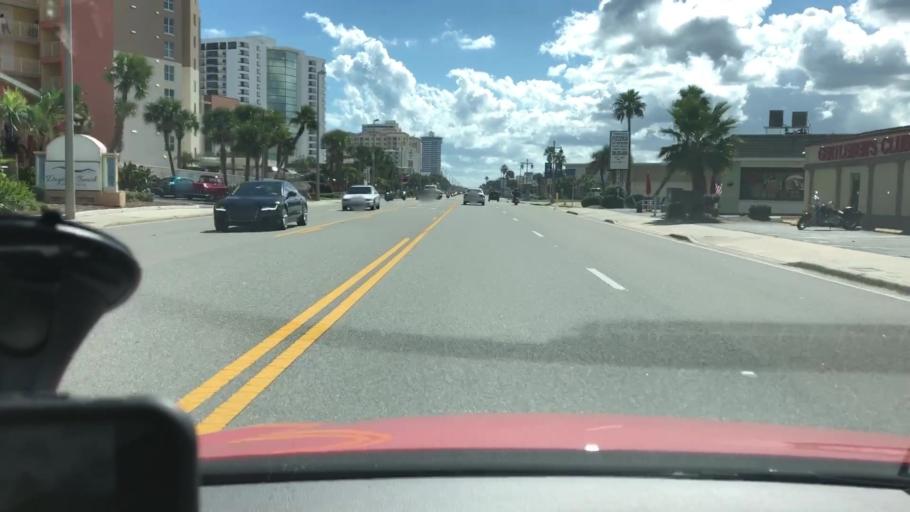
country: US
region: Florida
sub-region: Volusia County
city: Daytona Beach Shores
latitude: 29.1915
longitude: -80.9907
